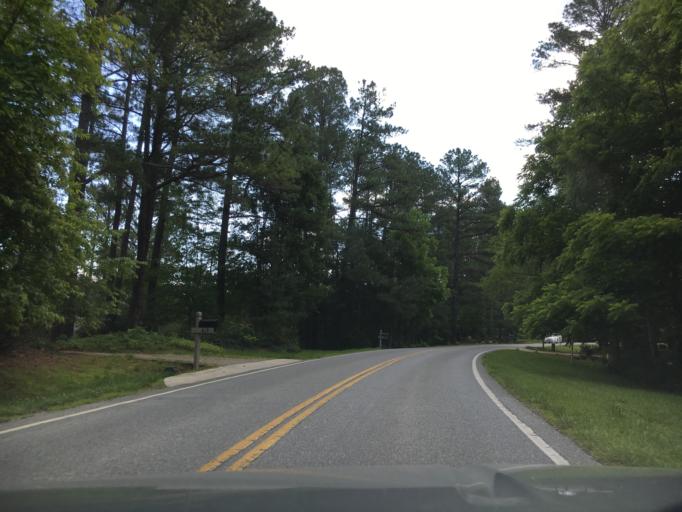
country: US
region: Virginia
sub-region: Bedford County
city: Forest
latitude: 37.3861
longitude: -79.2567
